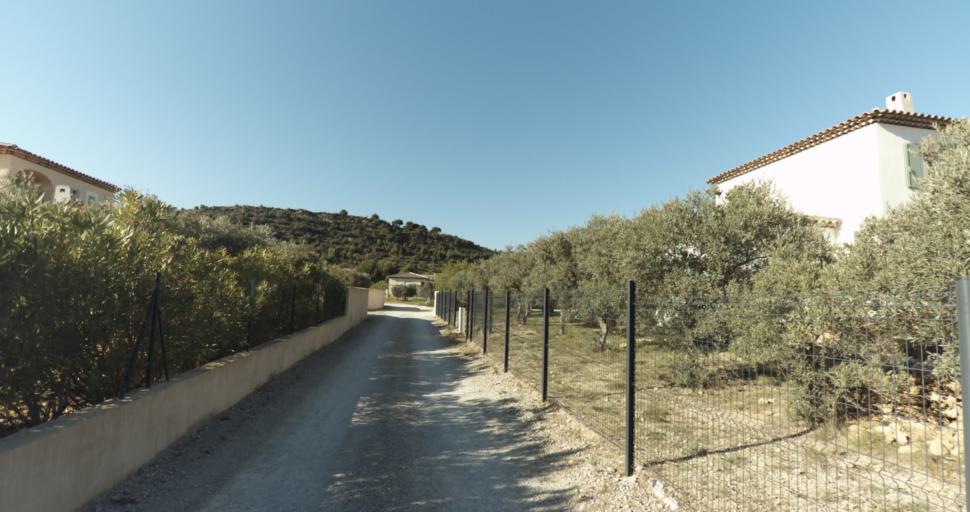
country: FR
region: Provence-Alpes-Cote d'Azur
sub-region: Departement des Bouches-du-Rhone
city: Pelissanne
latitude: 43.6426
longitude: 5.1483
